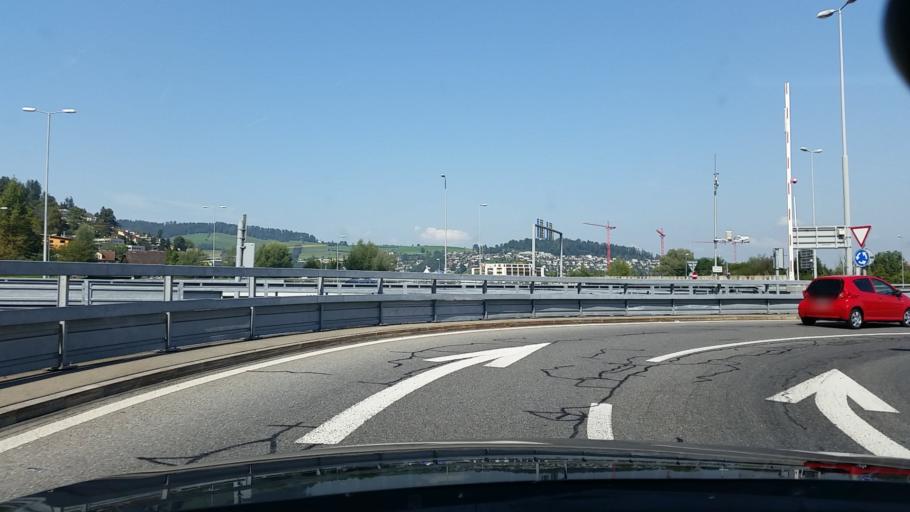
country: CH
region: Lucerne
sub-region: Lucerne-Land District
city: Horw
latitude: 47.0179
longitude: 8.2977
